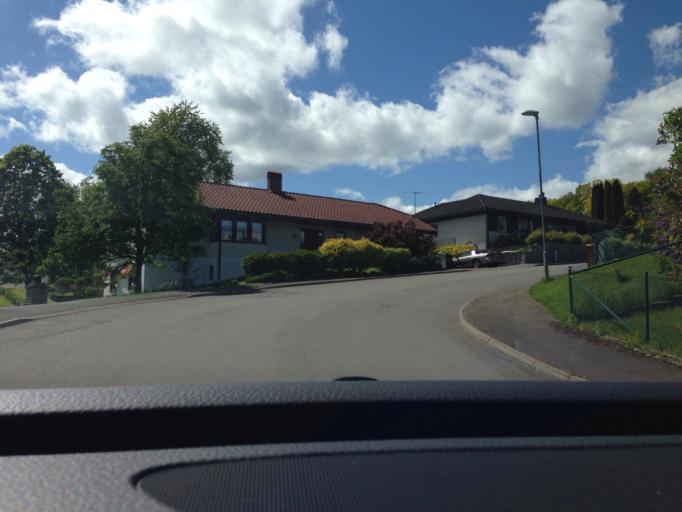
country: SE
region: Vaestra Goetaland
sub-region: Skovde Kommun
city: Skoevde
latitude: 58.4038
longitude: 13.8339
